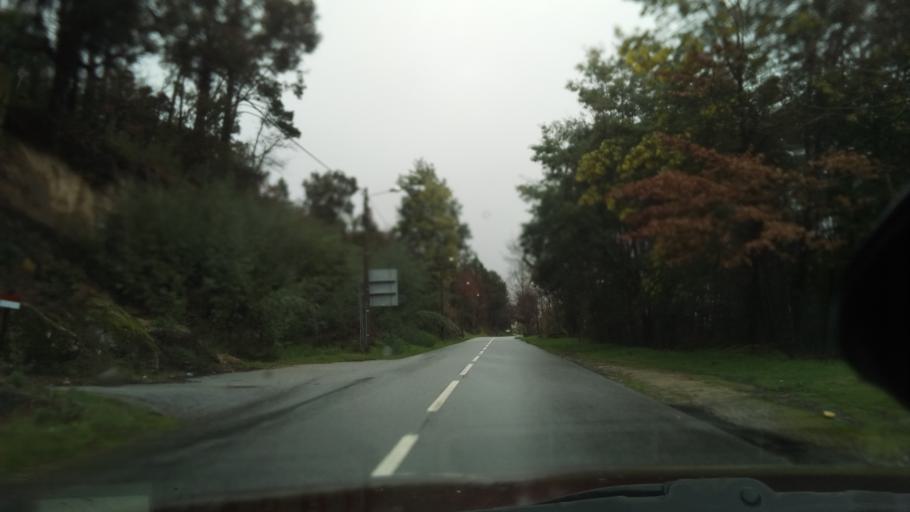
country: PT
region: Guarda
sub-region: Fornos de Algodres
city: Fornos de Algodres
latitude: 40.6251
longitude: -7.5403
